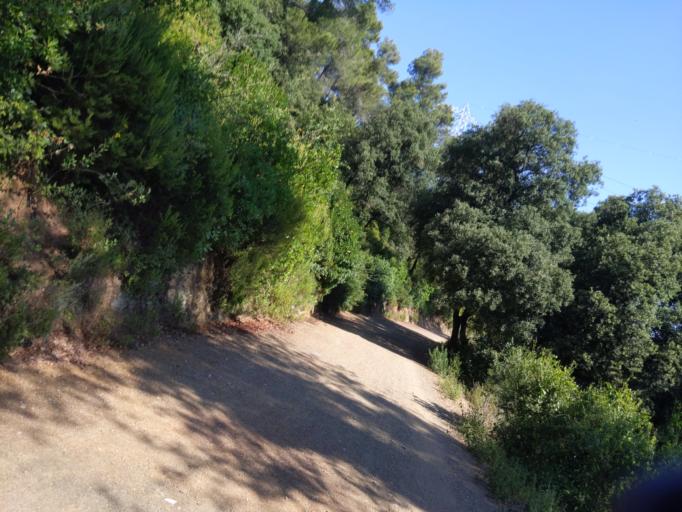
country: ES
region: Catalonia
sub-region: Provincia de Barcelona
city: Cerdanyola del Valles
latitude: 41.4600
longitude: 2.1367
